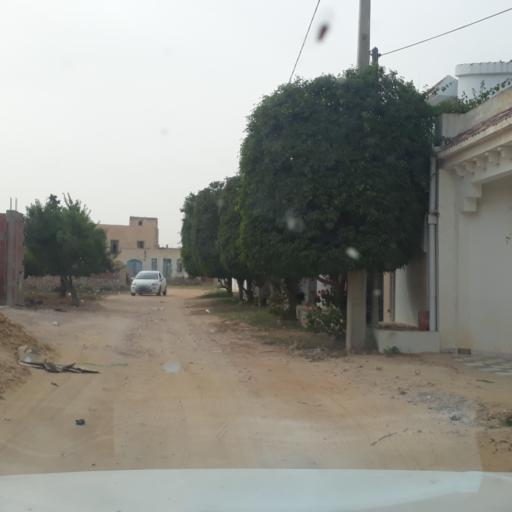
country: TN
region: Safaqis
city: Al Qarmadah
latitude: 34.8204
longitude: 10.7776
